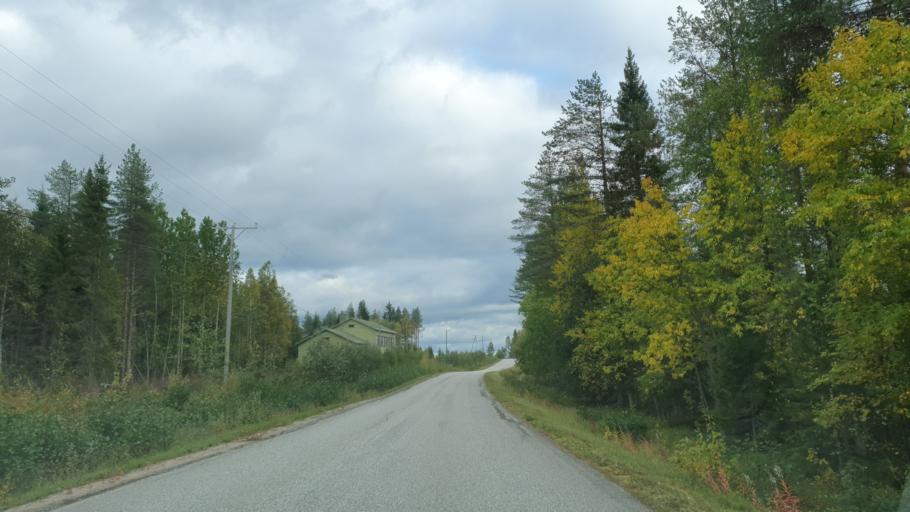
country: FI
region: Kainuu
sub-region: Kehys-Kainuu
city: Kuhmo
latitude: 63.9550
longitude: 29.7319
